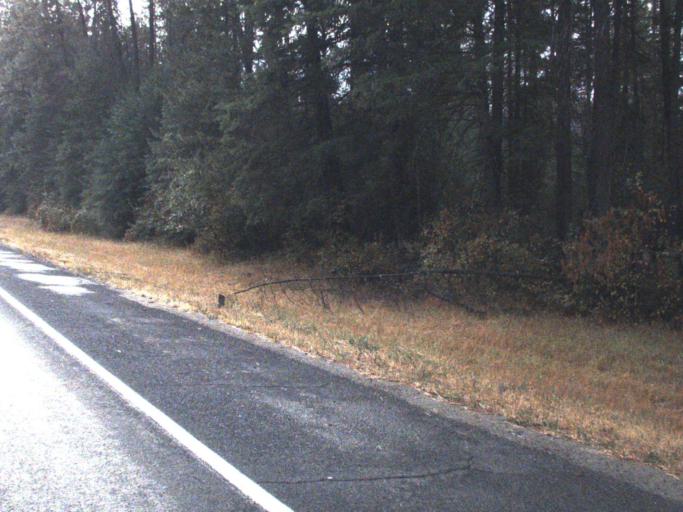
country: US
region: Washington
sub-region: Stevens County
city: Chewelah
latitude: 48.0636
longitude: -117.6801
